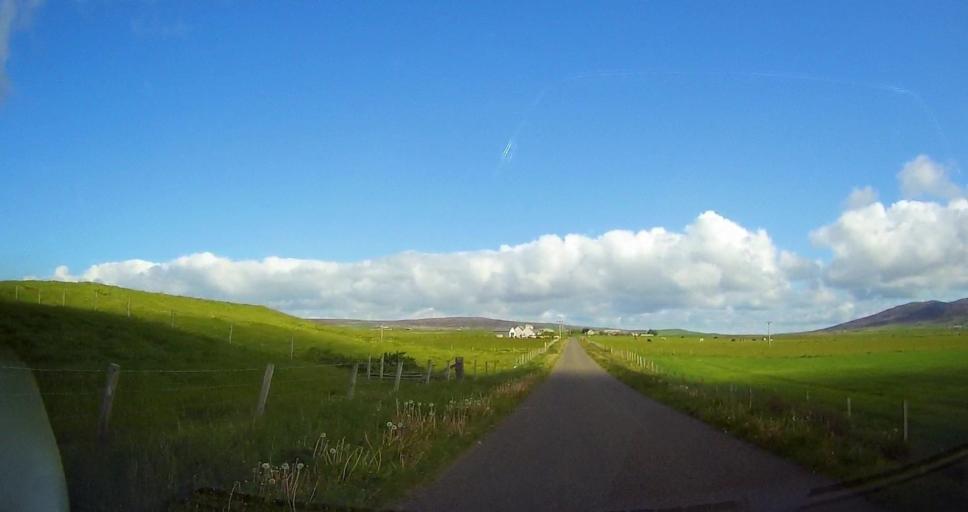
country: GB
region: Scotland
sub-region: Orkney Islands
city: Stromness
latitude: 58.9983
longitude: -3.1679
